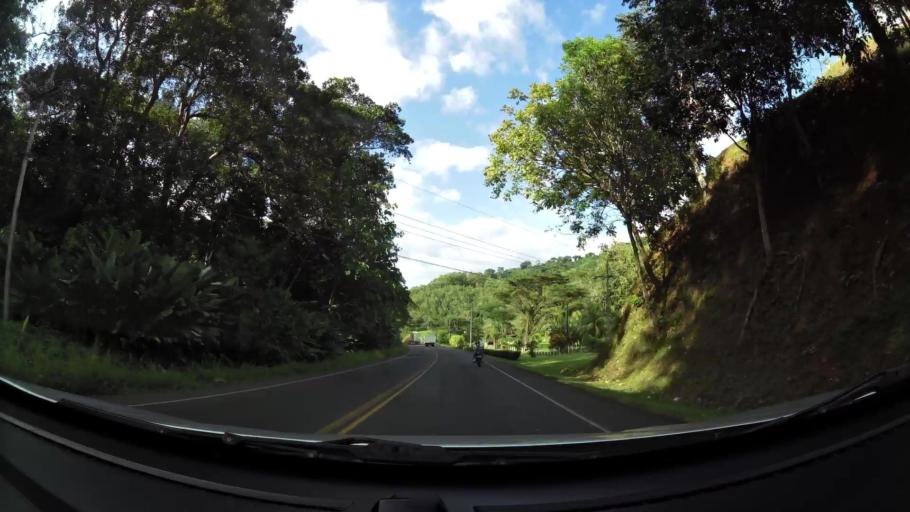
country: CR
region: Puntarenas
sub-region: Canton de Garabito
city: Jaco
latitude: 9.7283
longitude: -84.6261
